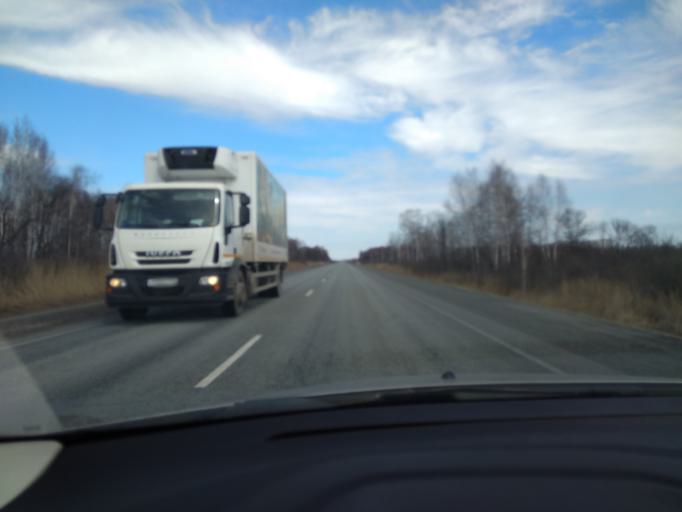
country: RU
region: Sverdlovsk
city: Pyshma
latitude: 57.0057
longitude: 63.3308
